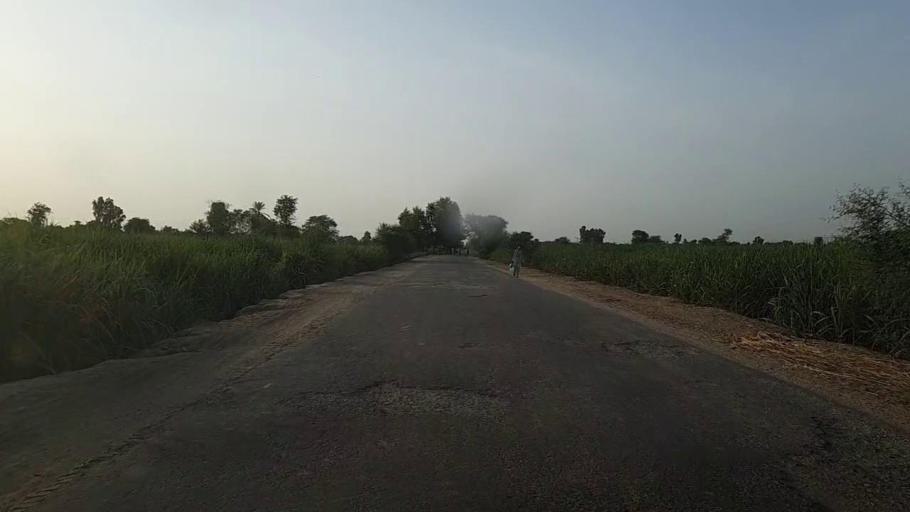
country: PK
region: Sindh
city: Ubauro
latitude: 28.1729
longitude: 69.8298
